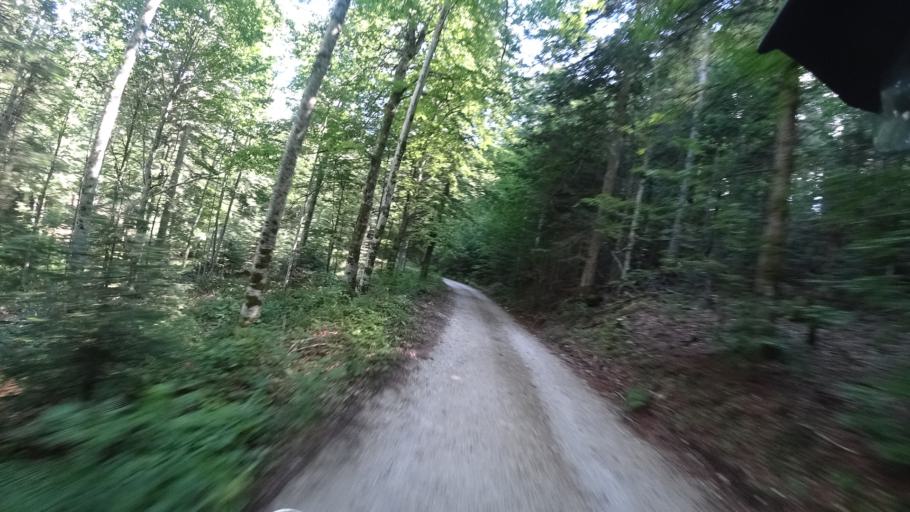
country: BA
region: Federation of Bosnia and Herzegovina
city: Orasac
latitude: 44.5007
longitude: 15.9460
